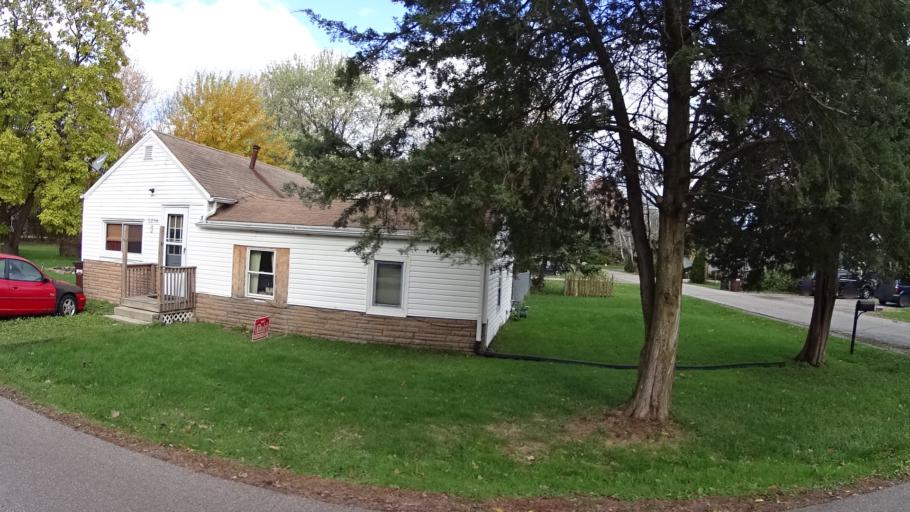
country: US
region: Ohio
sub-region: Lorain County
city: Sheffield
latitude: 41.4208
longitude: -82.1151
